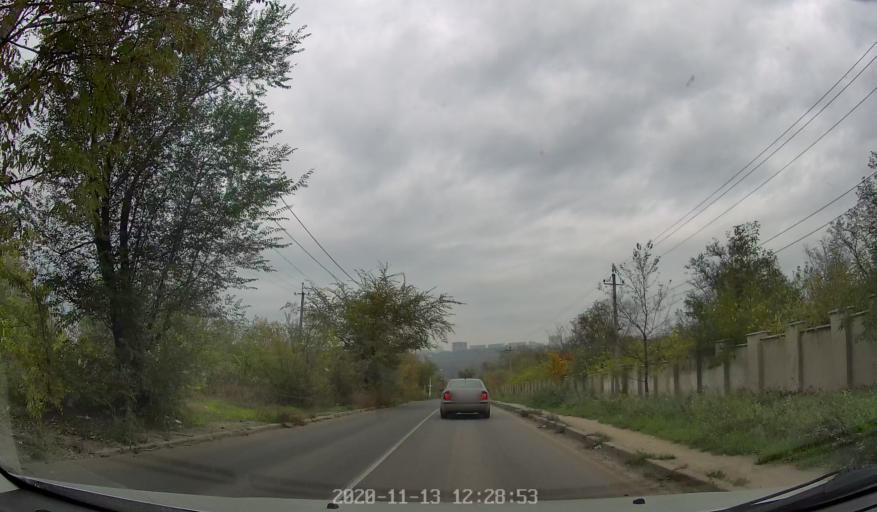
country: MD
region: Laloveni
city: Ialoveni
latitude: 46.9584
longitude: 28.8324
